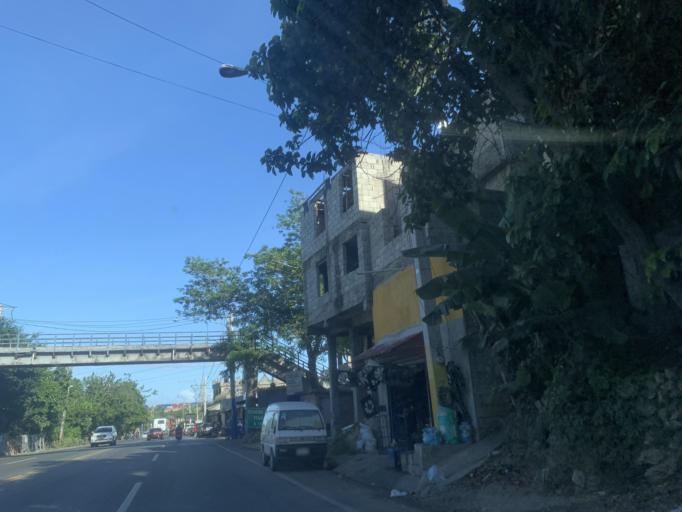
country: DO
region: San Cristobal
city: El Carril
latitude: 18.4339
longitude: -70.0107
